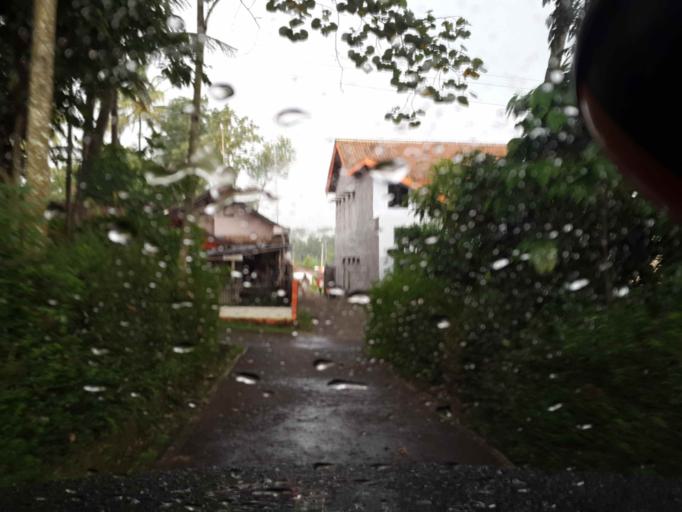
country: ID
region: Central Java
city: Salatiga
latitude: -7.3171
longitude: 110.4791
